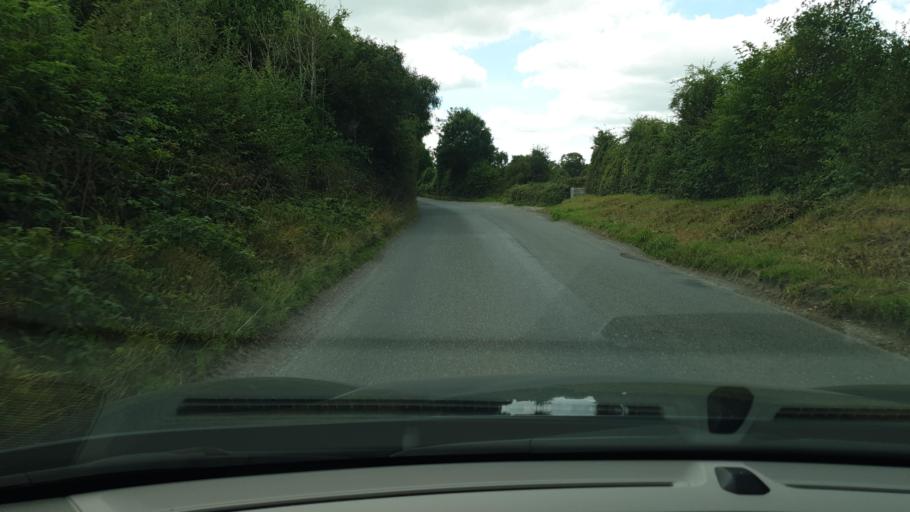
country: IE
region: Leinster
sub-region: An Mhi
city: Dunshaughlin
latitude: 53.5541
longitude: -6.6085
